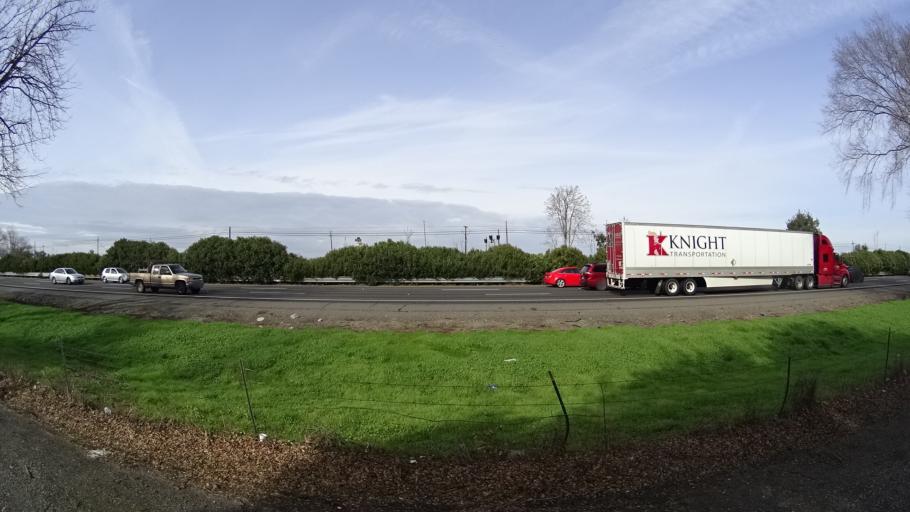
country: US
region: California
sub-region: Yolo County
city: Davis
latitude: 38.5569
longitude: -121.6751
